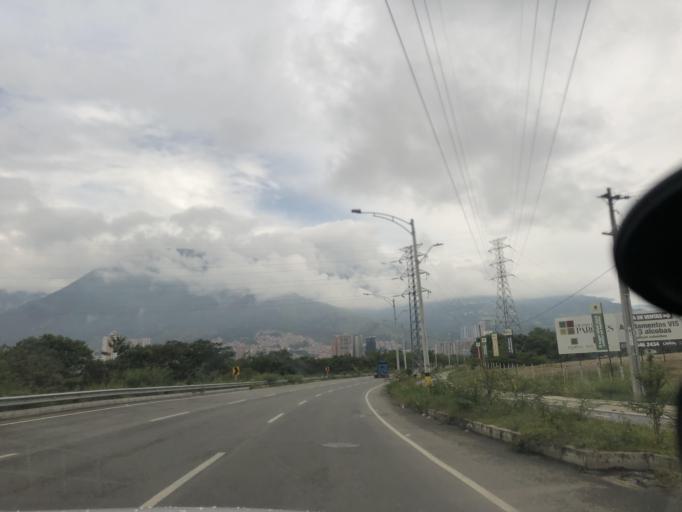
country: CO
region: Antioquia
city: Bello
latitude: 6.3230
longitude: -75.5534
